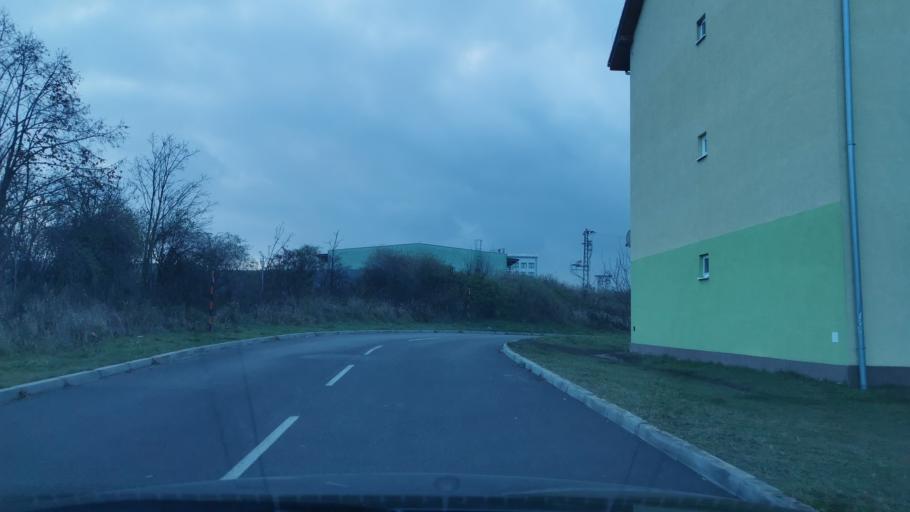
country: SK
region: Trnavsky
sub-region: Okres Skalica
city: Holic
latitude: 48.8032
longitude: 17.1559
